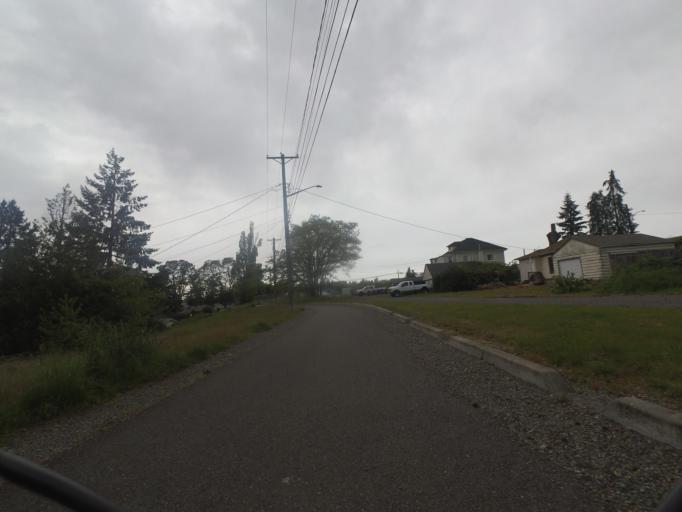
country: US
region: Washington
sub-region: Pierce County
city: Lakewood
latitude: 47.2021
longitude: -122.4763
